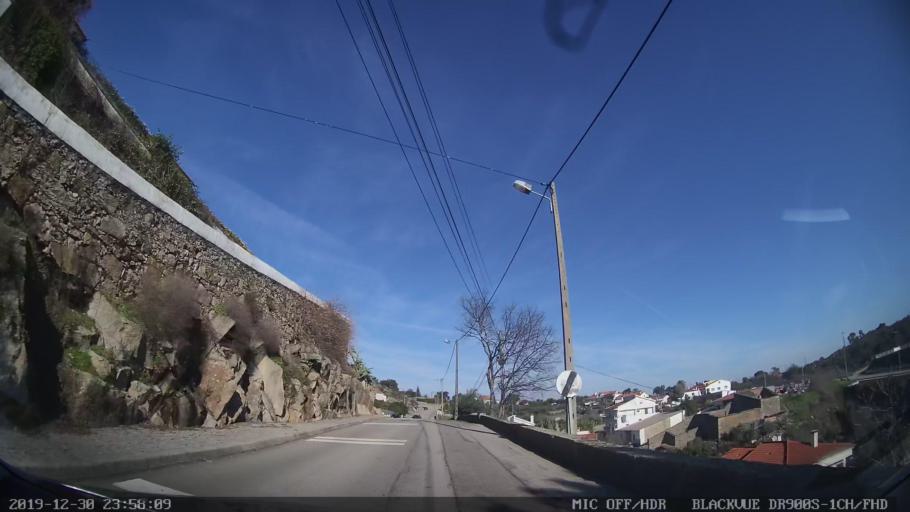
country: PT
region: Castelo Branco
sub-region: Idanha-A-Nova
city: Idanha-a-Nova
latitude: 39.9276
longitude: -7.2367
